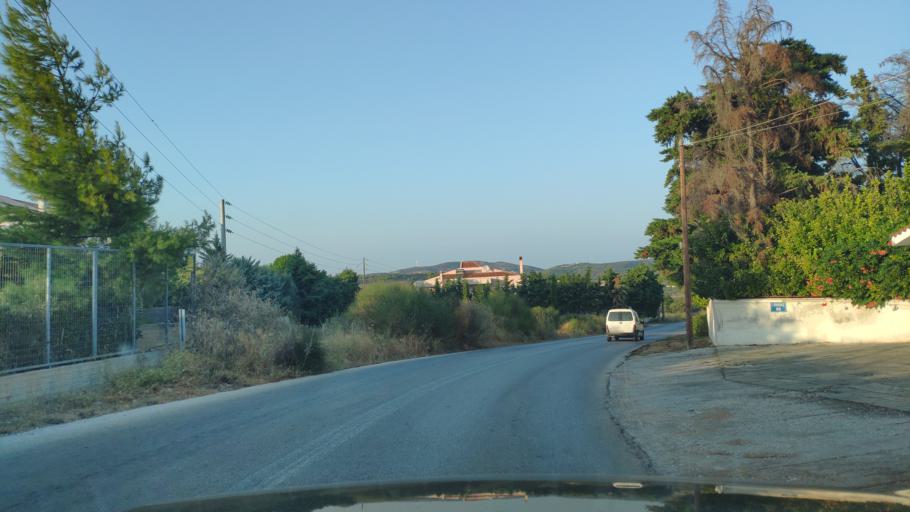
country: GR
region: Attica
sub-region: Nomarchia Anatolikis Attikis
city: Markopoulo
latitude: 37.9077
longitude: 23.9617
